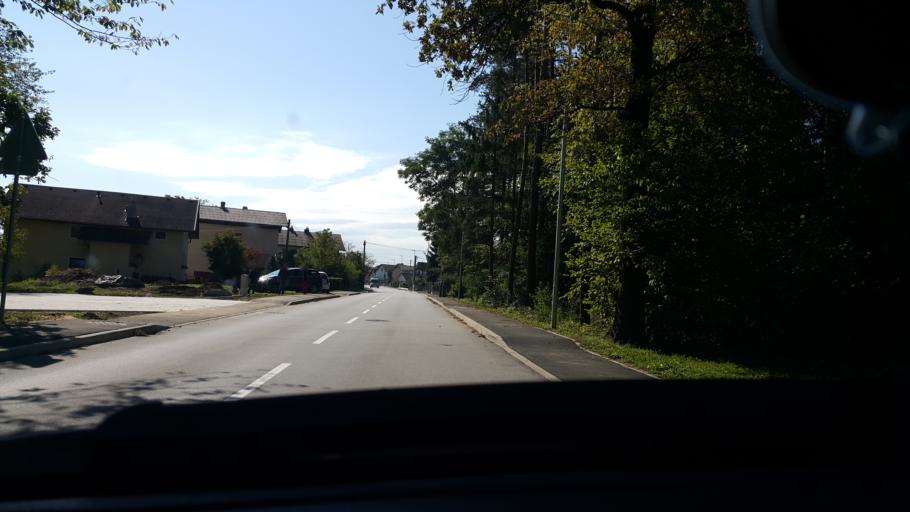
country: SI
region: Miklavz na Dravskem Polju
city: Miklavz na Dravskem Polju
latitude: 46.4860
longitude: 15.7003
